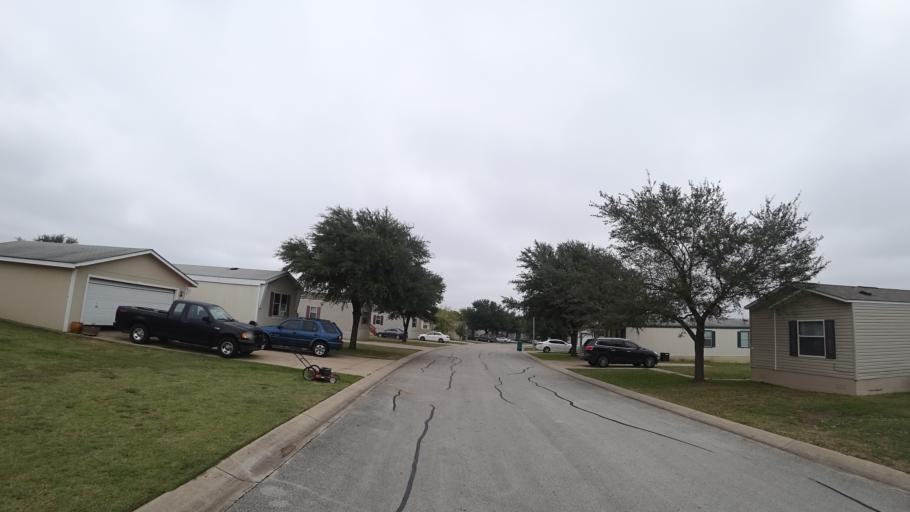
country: US
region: Texas
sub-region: Travis County
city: Pflugerville
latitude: 30.4124
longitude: -97.6040
